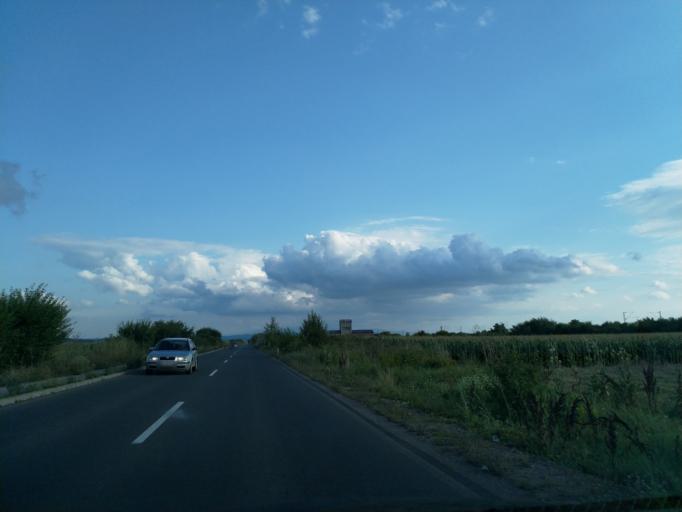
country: RS
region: Central Serbia
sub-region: Pomoravski Okrug
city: Paracin
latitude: 43.8237
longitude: 21.4180
